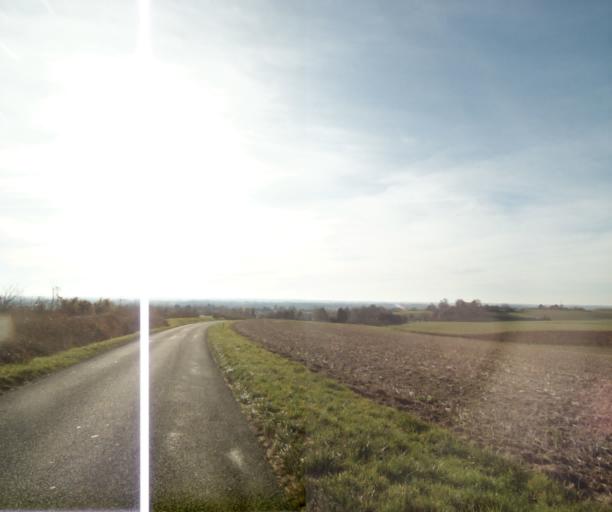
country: FR
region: Poitou-Charentes
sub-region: Departement de la Charente-Maritime
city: Chaniers
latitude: 45.7259
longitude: -0.5524
